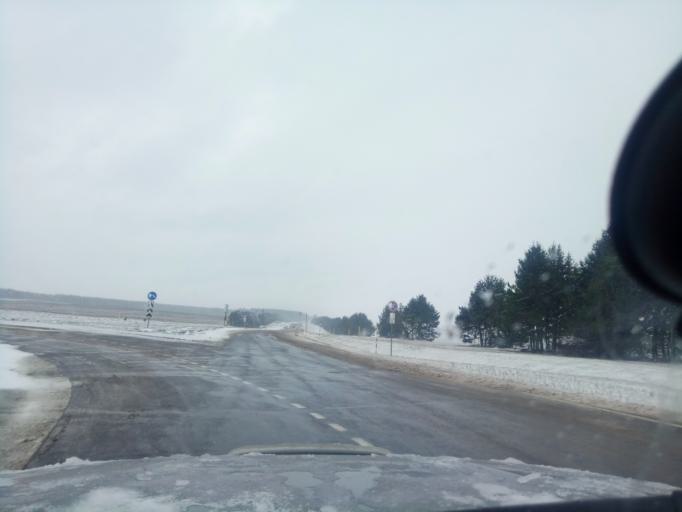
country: BY
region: Minsk
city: Haradzyeya
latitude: 53.2938
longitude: 26.5752
